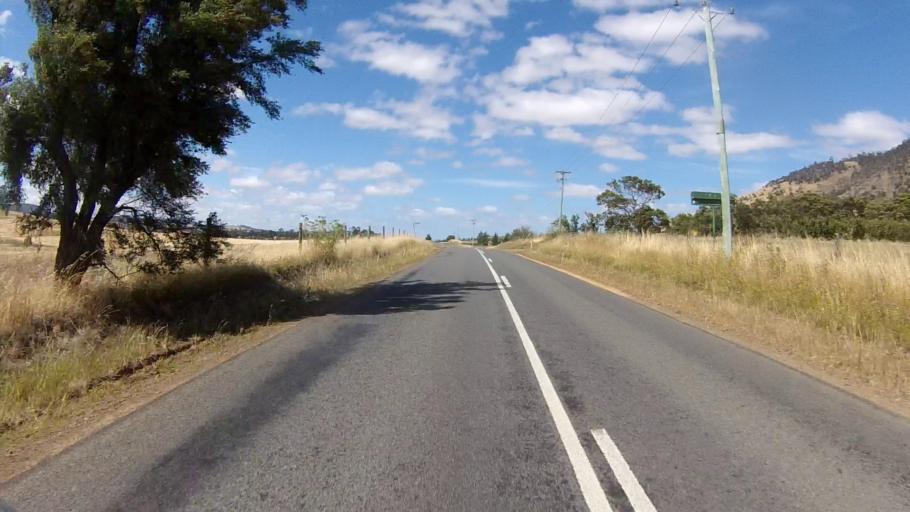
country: AU
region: Tasmania
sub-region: Sorell
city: Sorell
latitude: -42.6286
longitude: 147.4289
